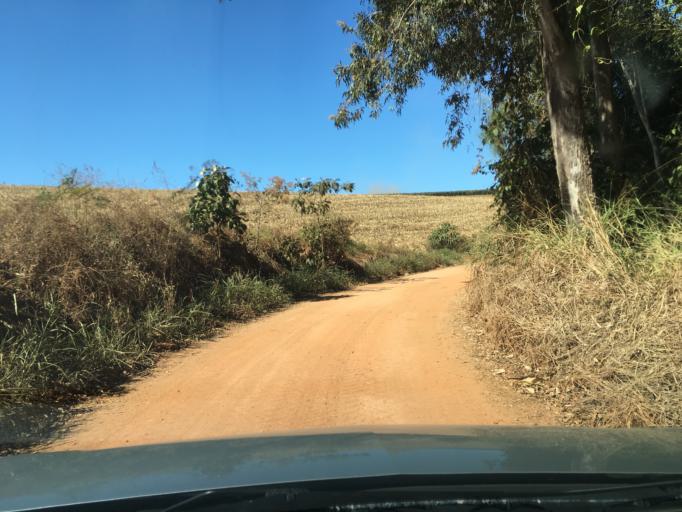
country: BR
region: Minas Gerais
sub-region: Campestre
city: Campestre
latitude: -21.5813
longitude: -46.2032
